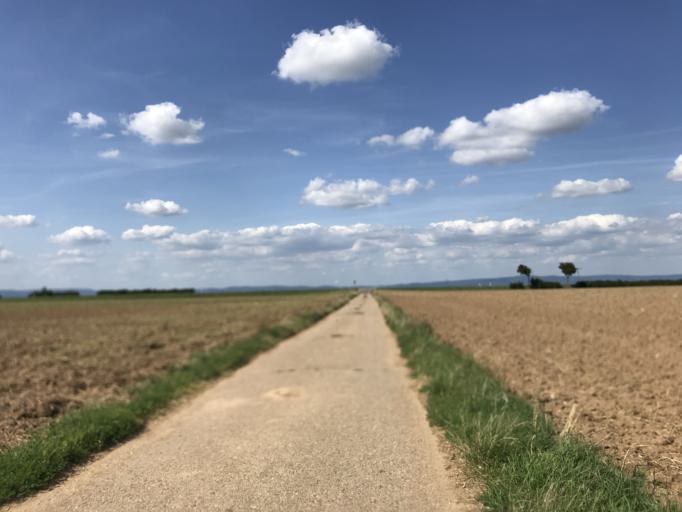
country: DE
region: Rheinland-Pfalz
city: Wolfsheim
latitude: 49.8847
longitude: 8.0359
